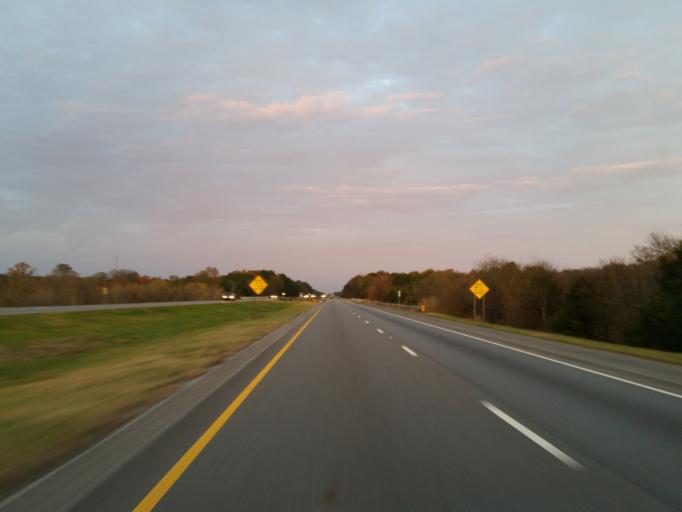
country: US
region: Alabama
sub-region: Sumter County
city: Livingston
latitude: 32.7157
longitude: -88.1258
